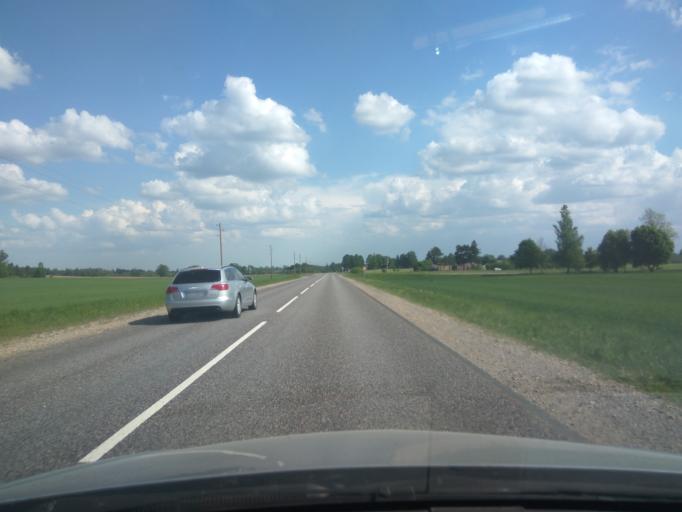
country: LV
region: Kuldigas Rajons
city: Kuldiga
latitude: 57.0242
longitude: 21.8623
